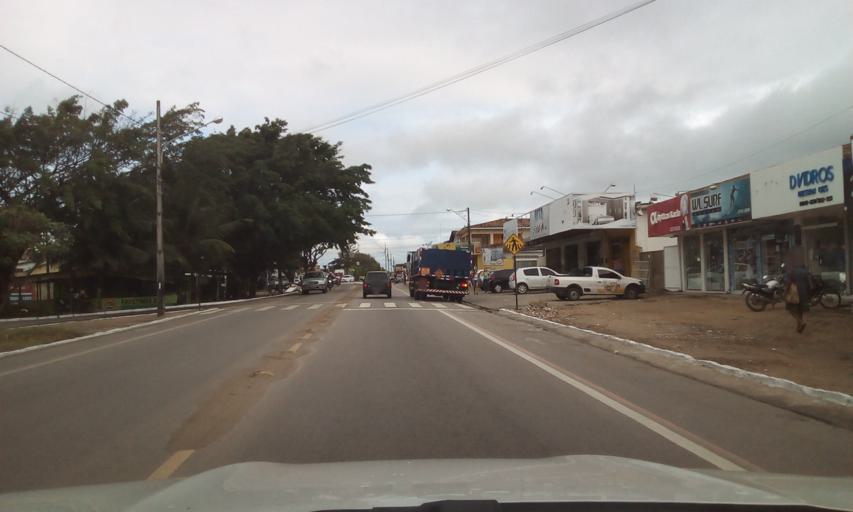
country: BR
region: Paraiba
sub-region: Conde
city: Conde
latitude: -7.1983
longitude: -34.8538
